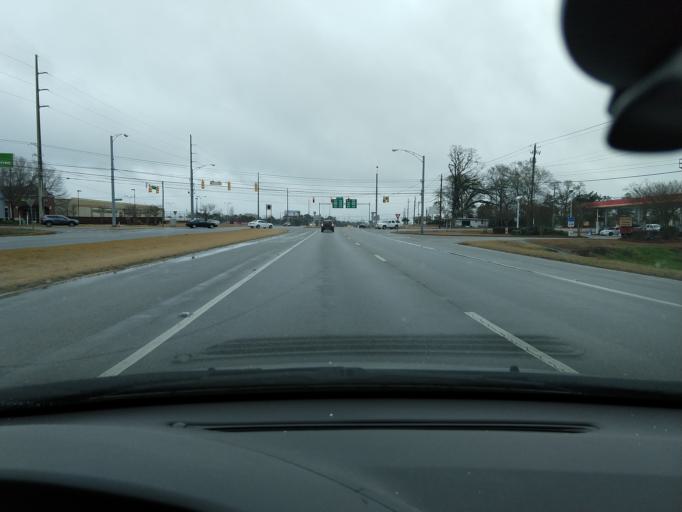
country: US
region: Alabama
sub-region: Houston County
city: Dothan
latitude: 31.2533
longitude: -85.3929
